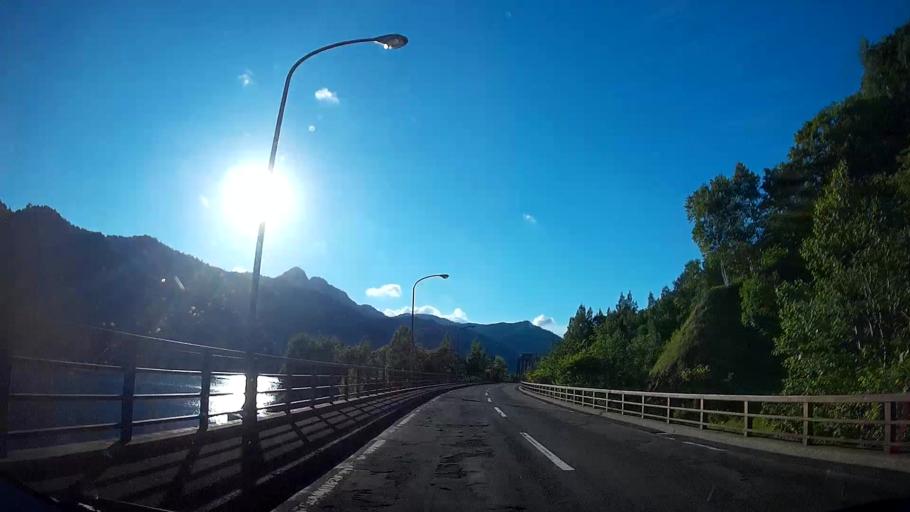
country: JP
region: Hokkaido
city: Sapporo
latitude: 42.9979
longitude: 141.1541
